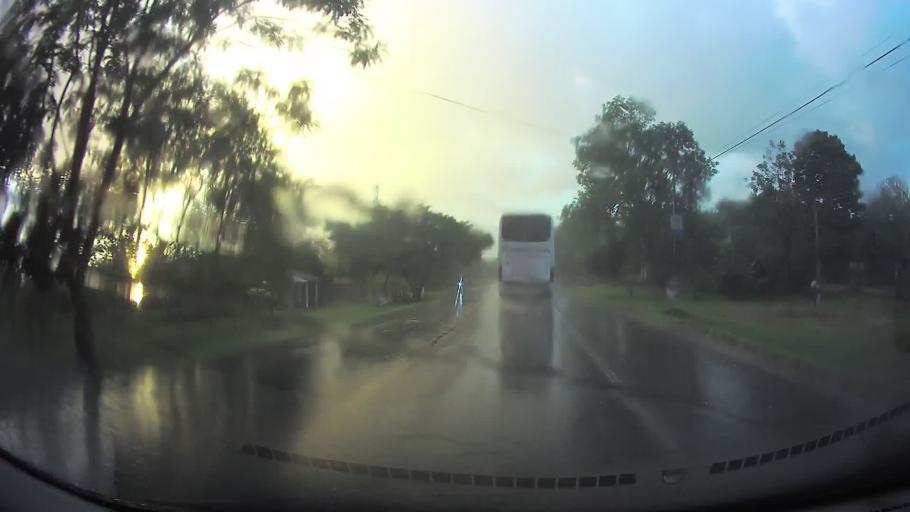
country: PY
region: Paraguari
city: Yaguaron
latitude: -25.5928
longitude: -57.2222
